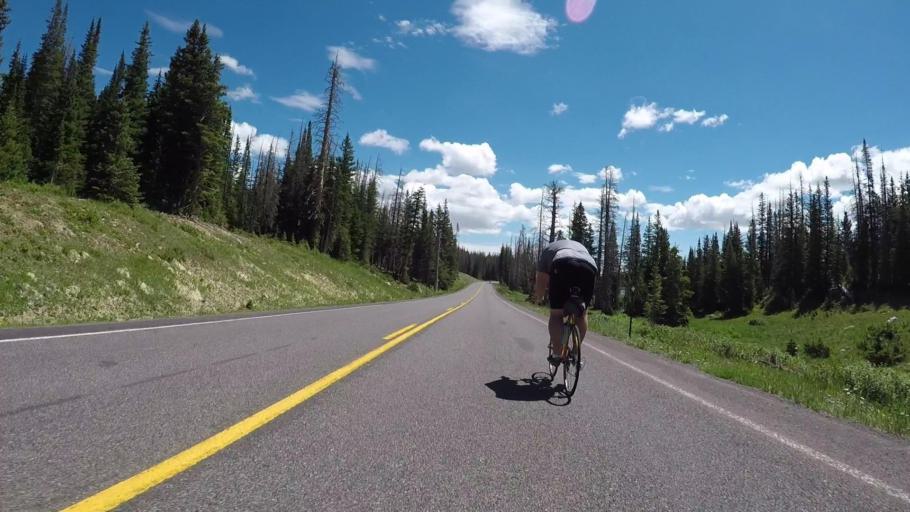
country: US
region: Wyoming
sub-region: Carbon County
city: Saratoga
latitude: 41.3518
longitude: -106.2687
